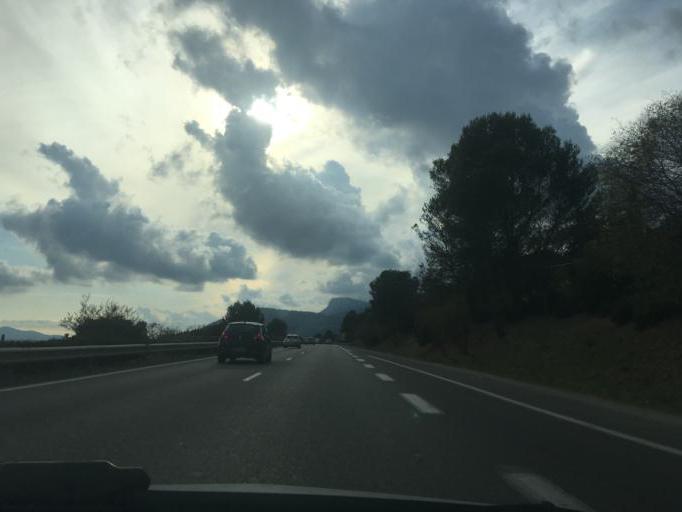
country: FR
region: Provence-Alpes-Cote d'Azur
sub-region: Departement du Var
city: Cuers
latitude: 43.2208
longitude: 6.0681
